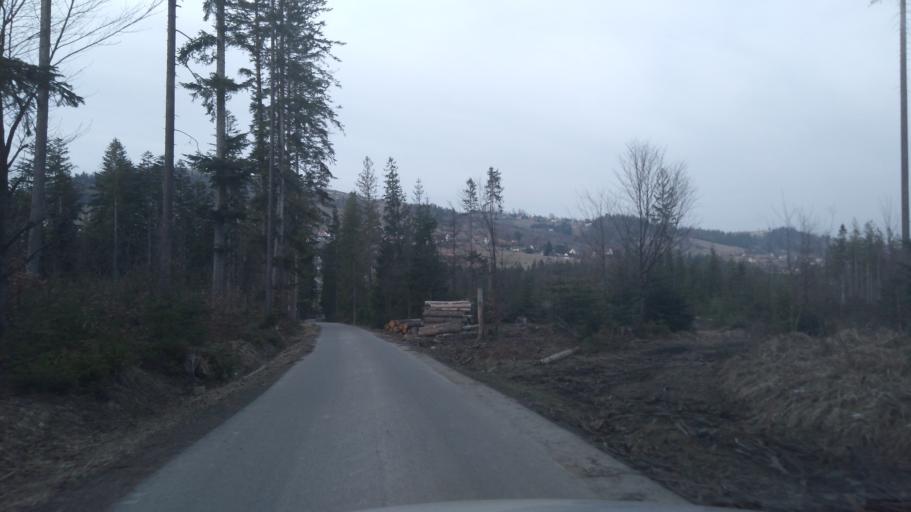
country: PL
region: Silesian Voivodeship
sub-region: Powiat cieszynski
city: Koniakow
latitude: 49.5321
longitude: 18.9510
